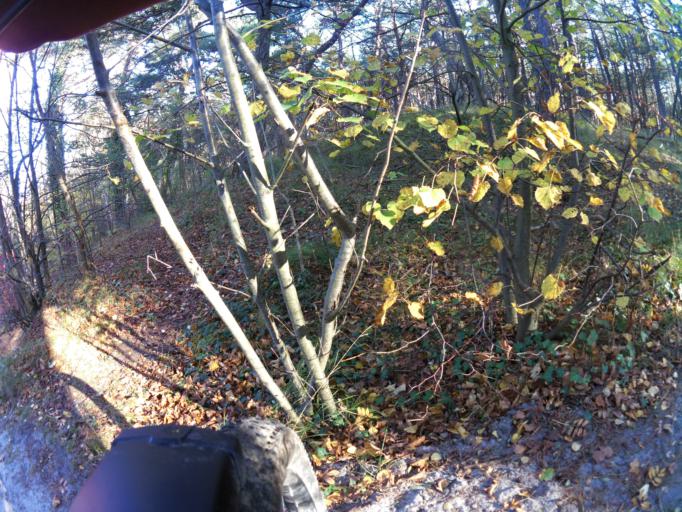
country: PL
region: Pomeranian Voivodeship
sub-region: Powiat pucki
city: Hel
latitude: 54.5997
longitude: 18.8131
